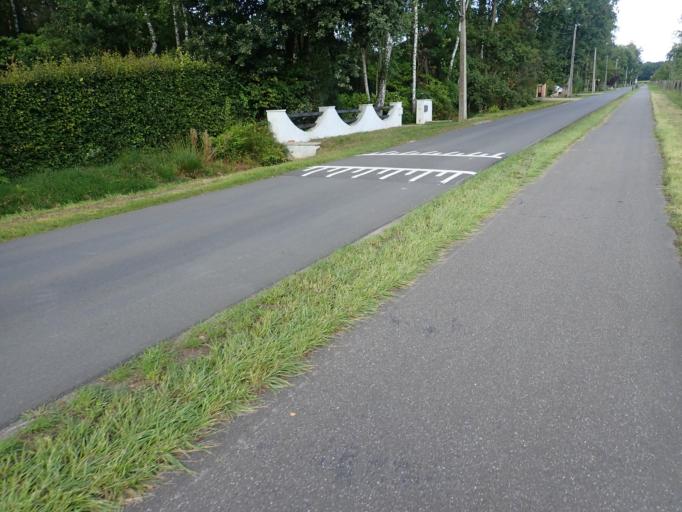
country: BE
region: Flanders
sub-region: Provincie Antwerpen
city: Zoersel
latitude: 51.2649
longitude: 4.6787
